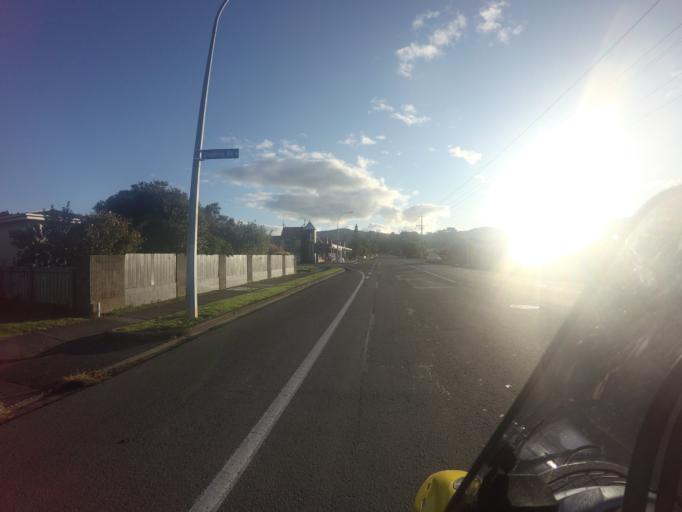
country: NZ
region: Gisborne
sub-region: Gisborne District
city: Gisborne
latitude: -38.6690
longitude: 178.0477
